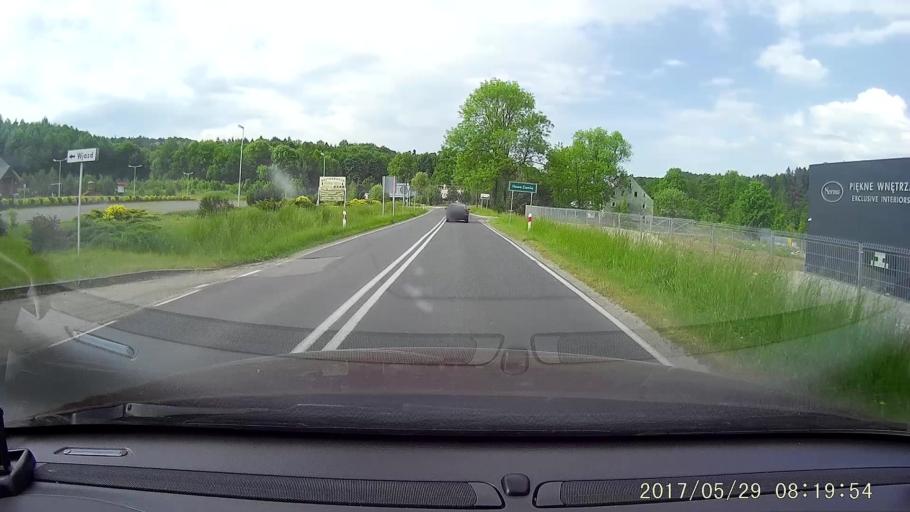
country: PL
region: Lower Silesian Voivodeship
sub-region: Powiat zlotoryjski
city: Zlotoryja
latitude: 51.0992
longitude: 15.8794
